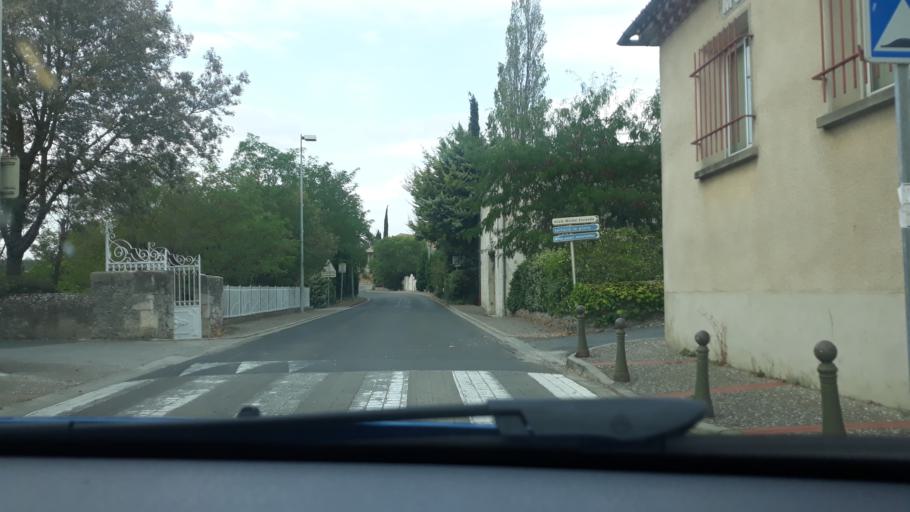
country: FR
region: Languedoc-Roussillon
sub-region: Departement de l'Aude
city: Pezens
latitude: 43.2801
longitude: 2.2301
